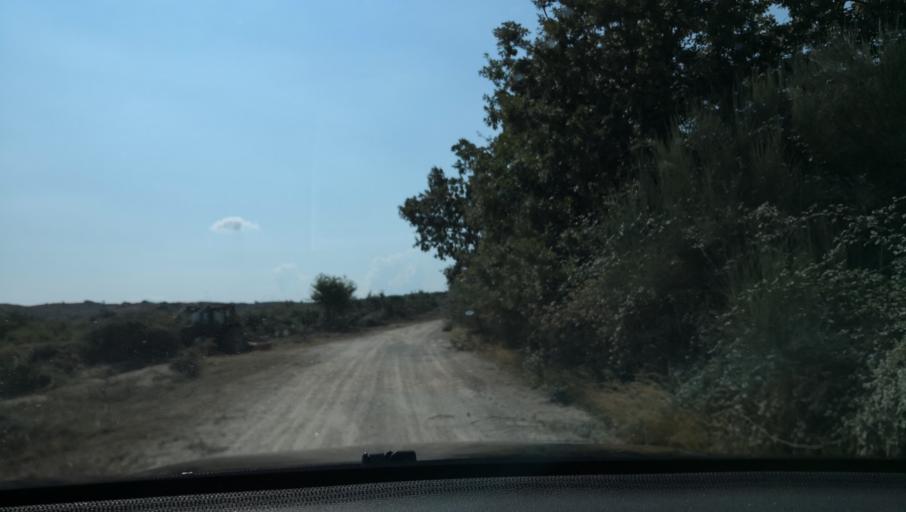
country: PT
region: Vila Real
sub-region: Sabrosa
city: Sabrosa
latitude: 41.3176
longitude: -7.6205
